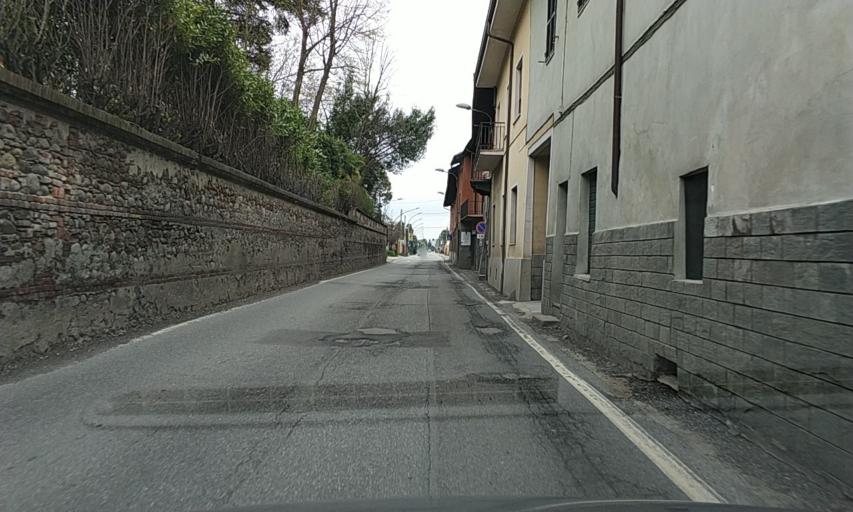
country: IT
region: Piedmont
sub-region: Provincia di Torino
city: Favria
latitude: 45.3313
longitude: 7.6926
